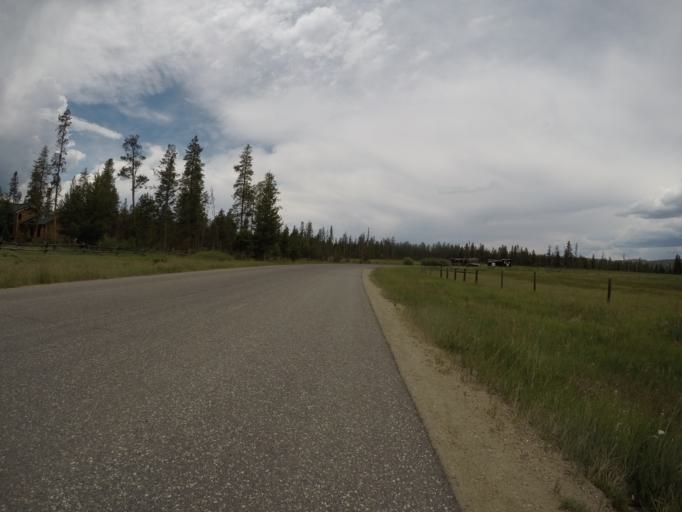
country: US
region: Colorado
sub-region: Grand County
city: Fraser
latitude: 39.9734
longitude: -105.8634
